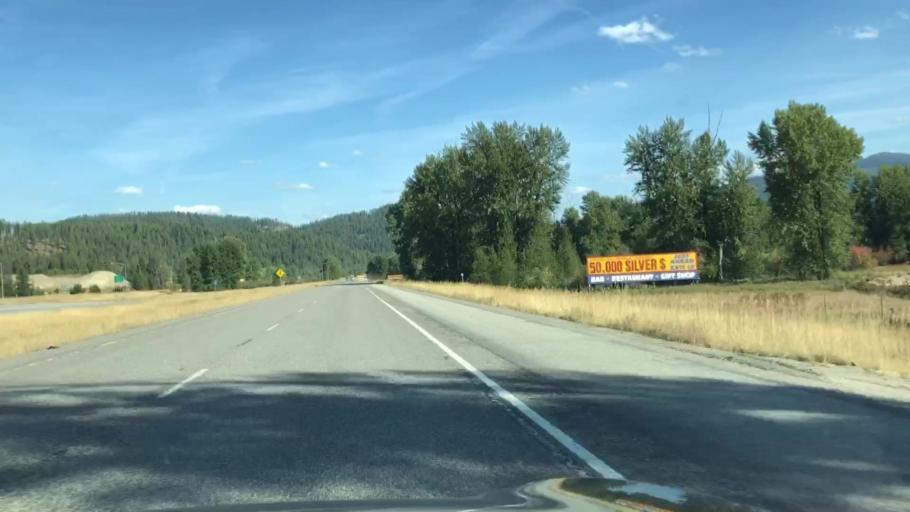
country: US
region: Montana
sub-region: Sanders County
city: Thompson Falls
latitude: 47.3927
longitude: -115.4222
